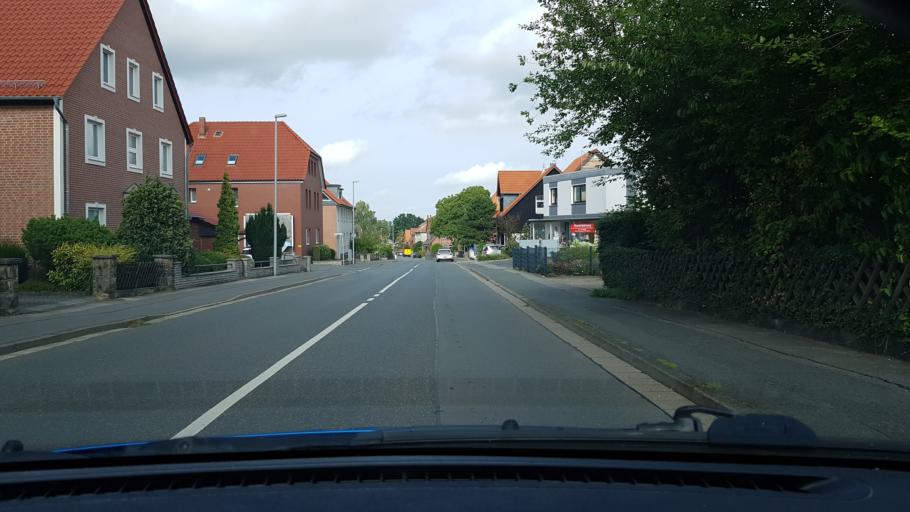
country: DE
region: Lower Saxony
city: Egestorf
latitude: 52.2931
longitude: 9.4905
